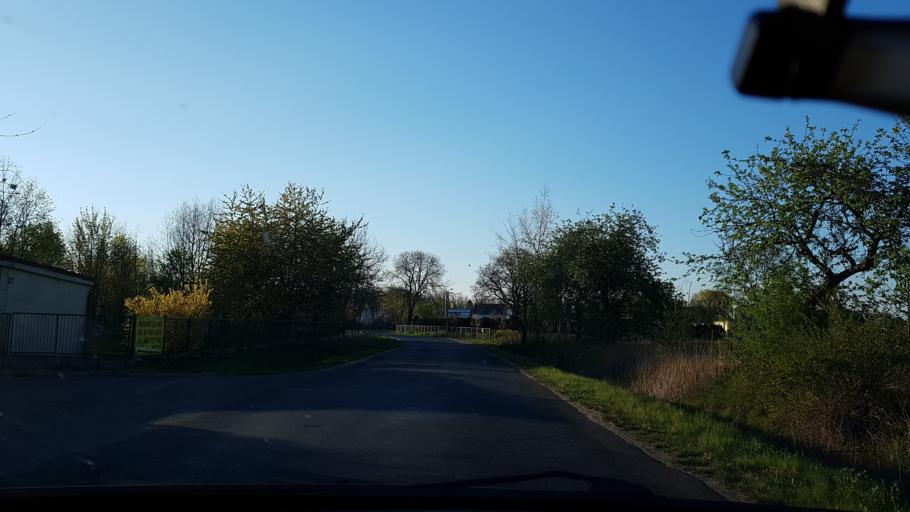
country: PL
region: Opole Voivodeship
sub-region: Powiat nyski
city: Nysa
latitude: 50.4284
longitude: 17.3070
